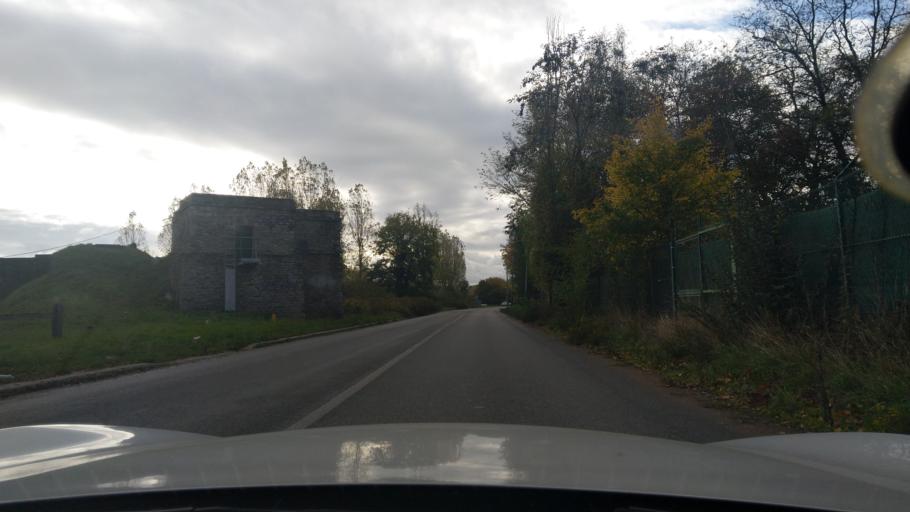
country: FR
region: Ile-de-France
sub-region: Departement de l'Essonne
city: Courcouronnes
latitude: 48.6294
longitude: 2.3970
